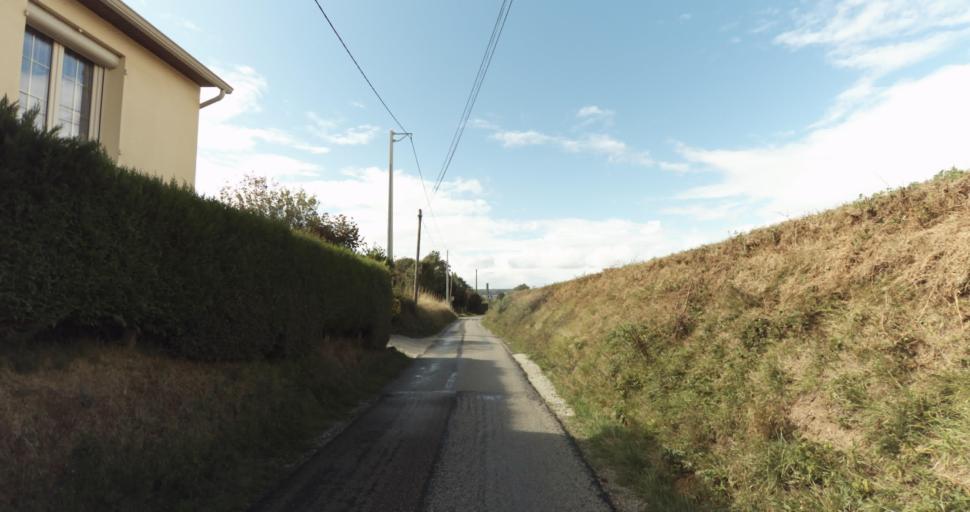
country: FR
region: Lower Normandy
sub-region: Departement de l'Orne
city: Gace
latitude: 48.7900
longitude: 0.3065
